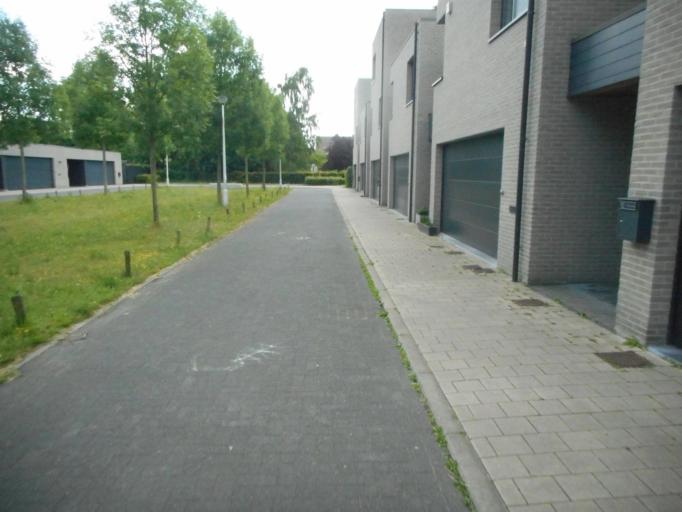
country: BE
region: Flanders
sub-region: Provincie Antwerpen
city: Brasschaat
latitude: 51.3089
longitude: 4.4904
